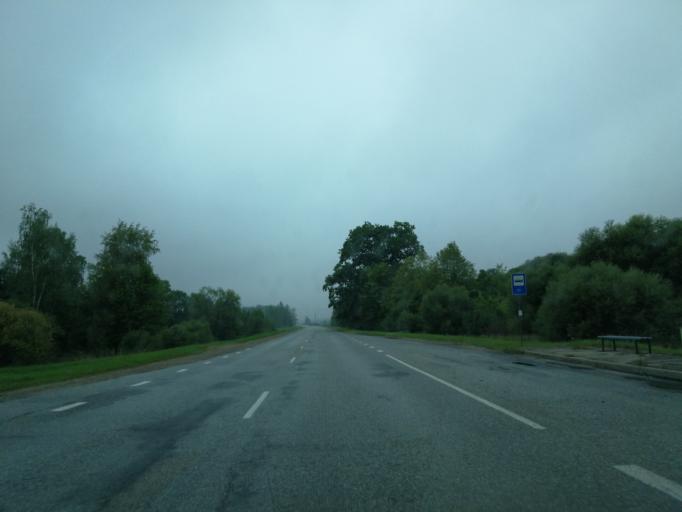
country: LV
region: Varkava
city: Vecvarkava
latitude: 56.3127
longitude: 26.5371
